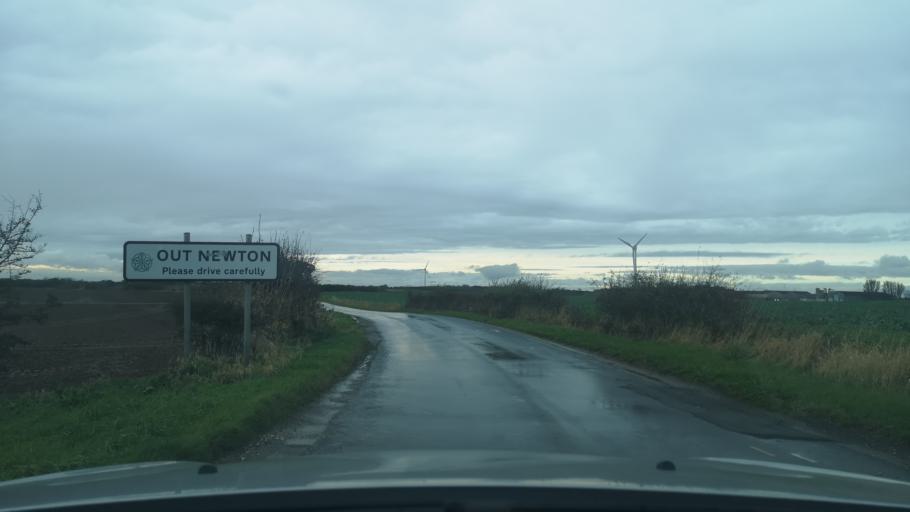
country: GB
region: England
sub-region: East Riding of Yorkshire
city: Easington
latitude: 53.6642
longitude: 0.0936
